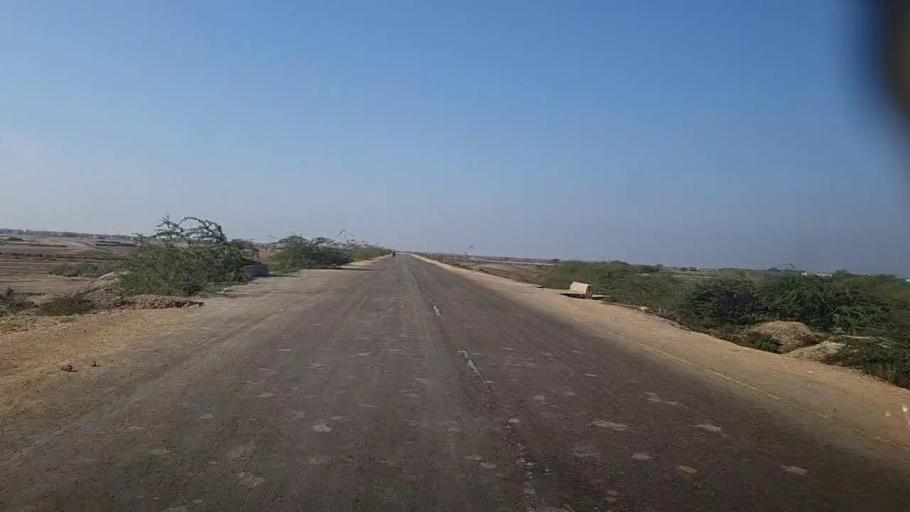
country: PK
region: Sindh
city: Mirpur Sakro
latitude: 24.5565
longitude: 67.4946
